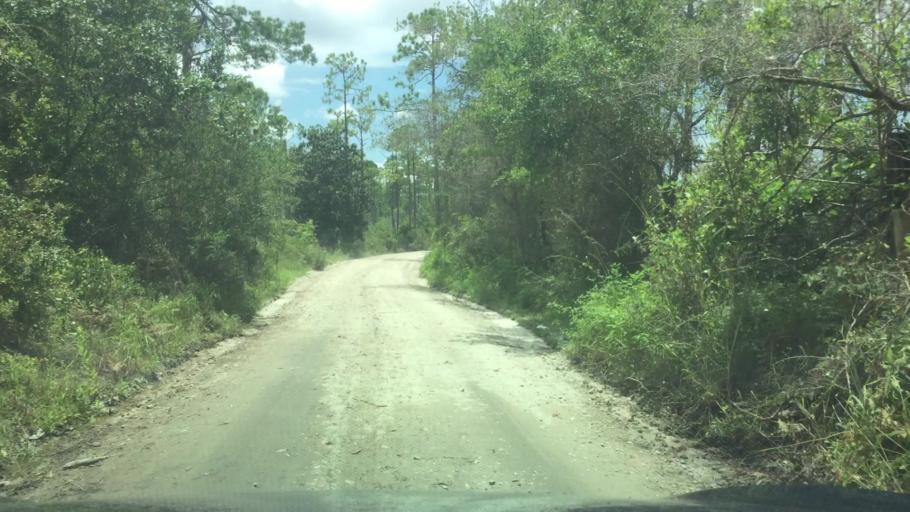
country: US
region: Florida
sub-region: Bay County
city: Mexico Beach
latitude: 29.9644
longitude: -85.4480
